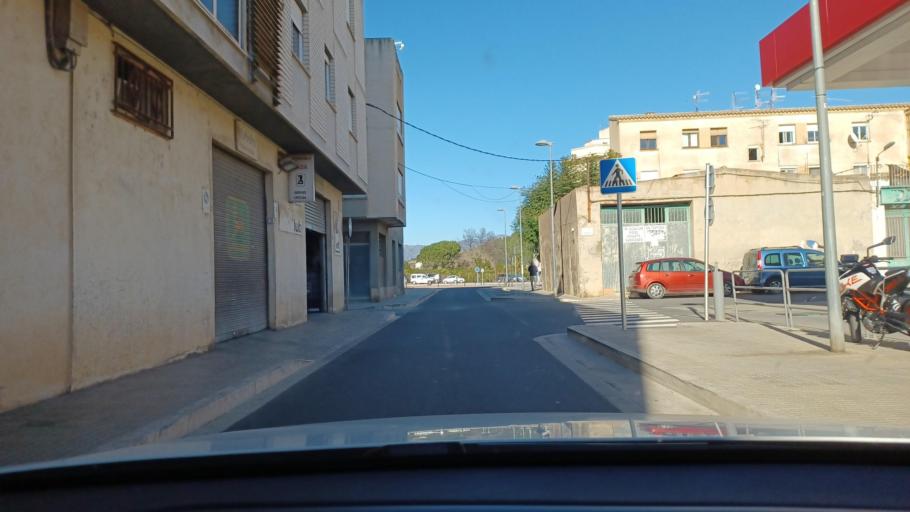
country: ES
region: Catalonia
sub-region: Provincia de Tarragona
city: Tortosa
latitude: 40.8193
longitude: 0.5238
